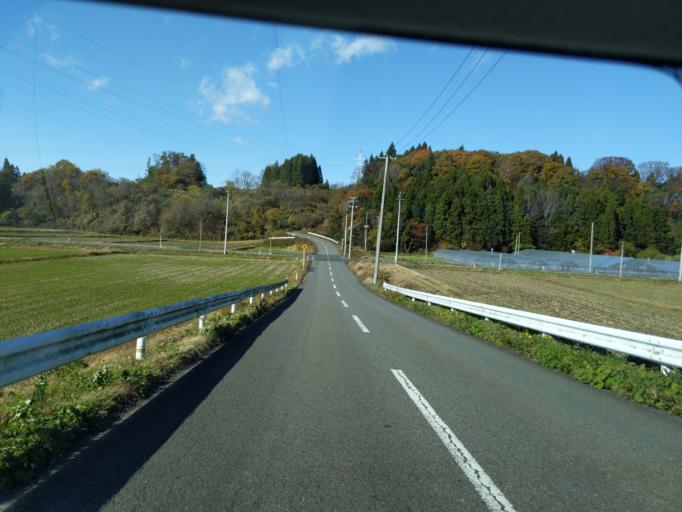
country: JP
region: Iwate
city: Mizusawa
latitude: 39.0911
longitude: 141.1255
